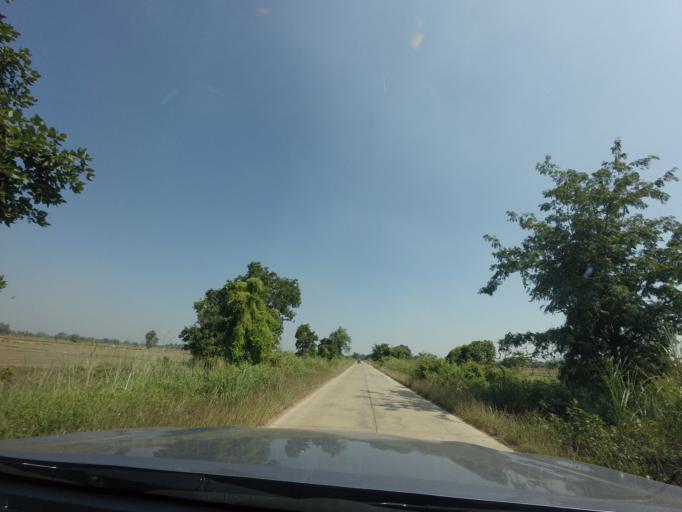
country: TH
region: Sukhothai
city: Sawankhalok
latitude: 17.2750
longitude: 99.8113
